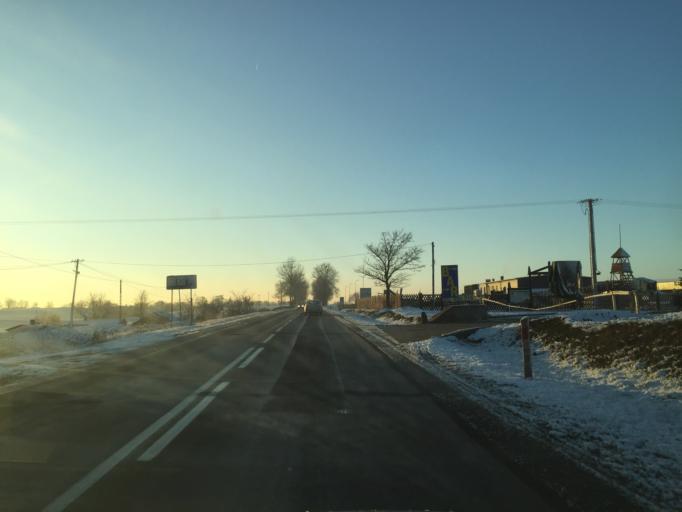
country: PL
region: Kujawsko-Pomorskie
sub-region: Powiat wabrzeski
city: Debowa Laka
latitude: 53.1899
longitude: 19.0584
